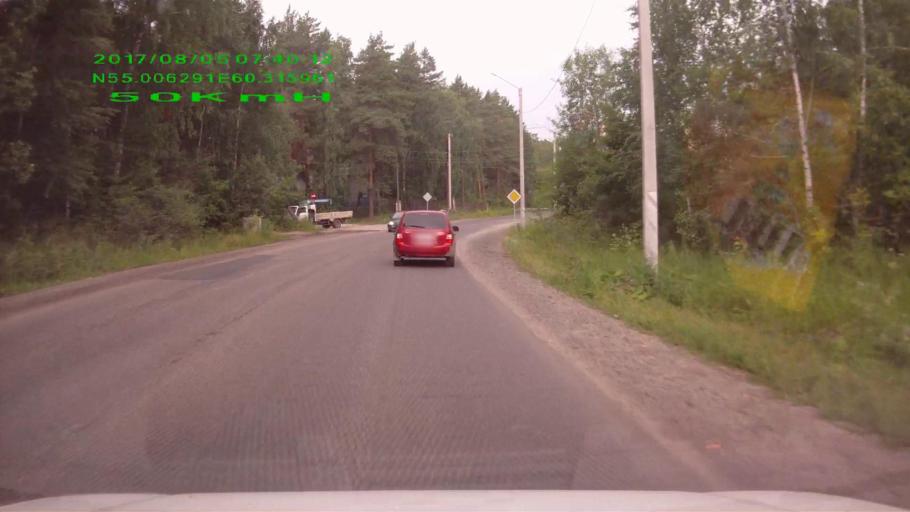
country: RU
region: Chelyabinsk
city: Chebarkul'
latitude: 55.0064
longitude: 60.3156
